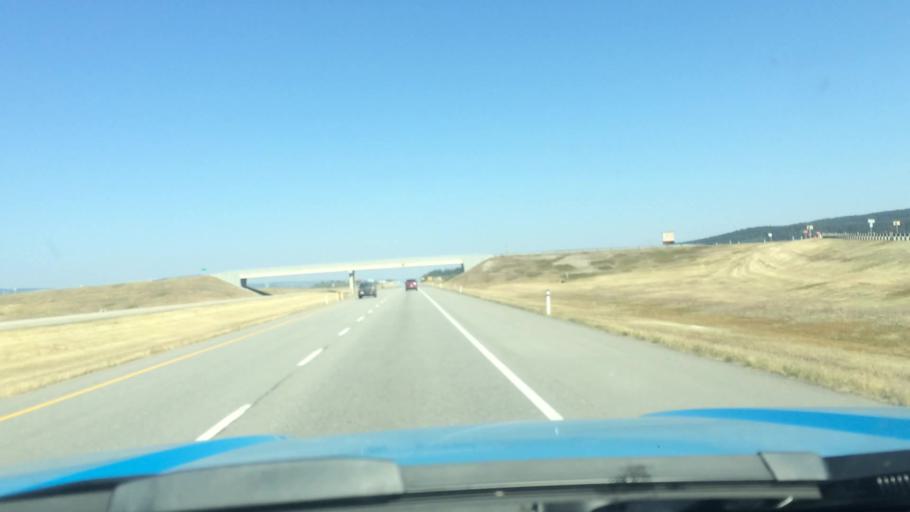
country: CA
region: Alberta
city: Canmore
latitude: 51.1024
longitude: -115.0236
